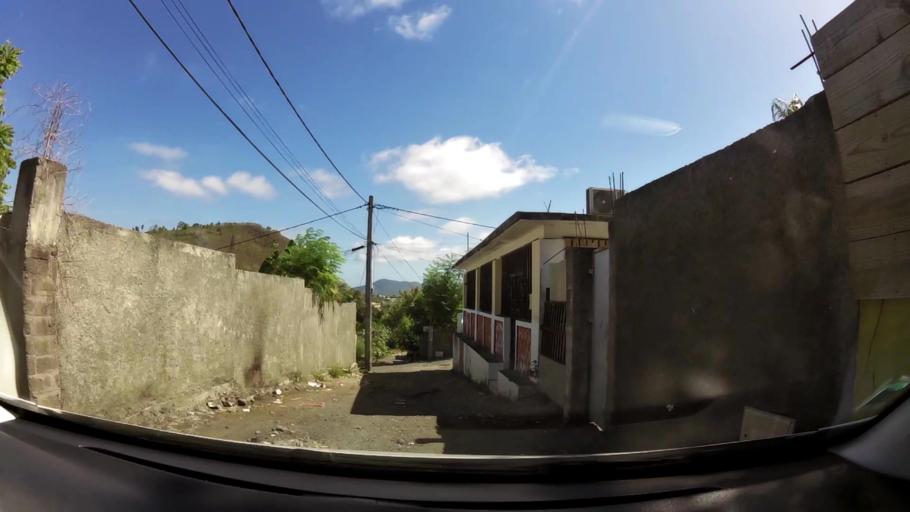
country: YT
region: Pamandzi
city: Pamandzi
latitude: -12.7873
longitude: 45.2801
